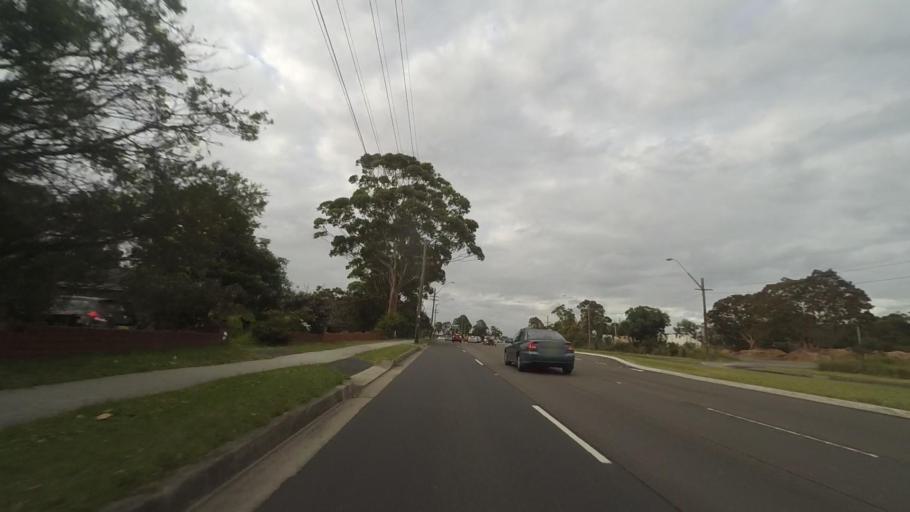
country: AU
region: New South Wales
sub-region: Sutherland Shire
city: Heathcote
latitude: -34.0811
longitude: 151.0107
